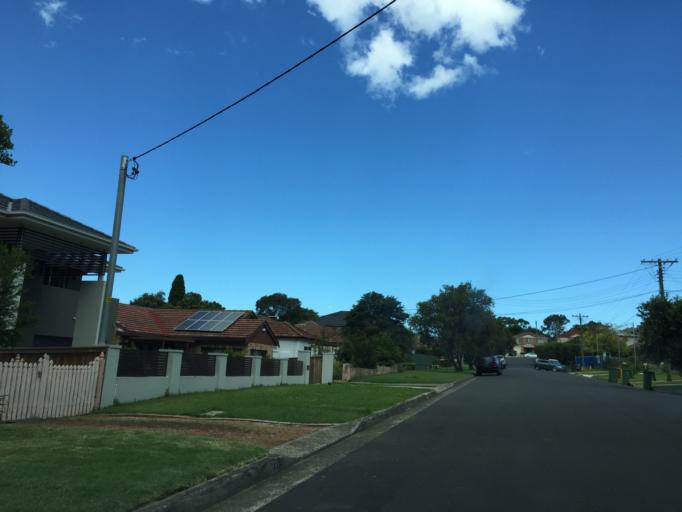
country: AU
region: New South Wales
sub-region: Parramatta
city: Dundas Valley
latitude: -33.7866
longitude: 151.0658
